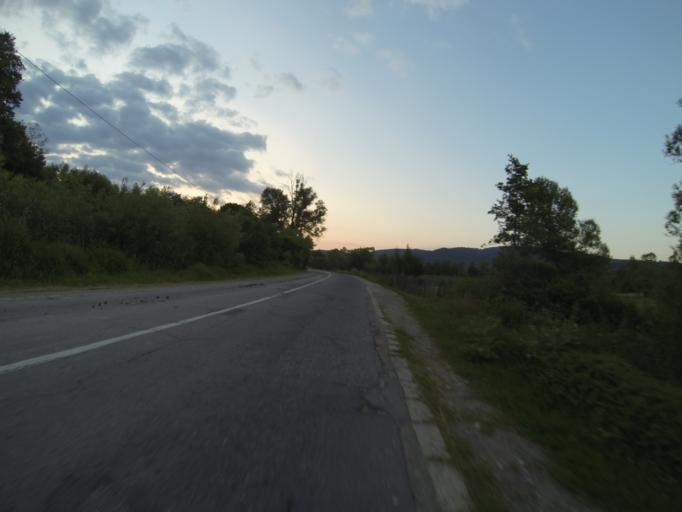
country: RO
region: Brasov
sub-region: Comuna Sinca Noua
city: Sinca Noua
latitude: 45.7150
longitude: 25.2415
